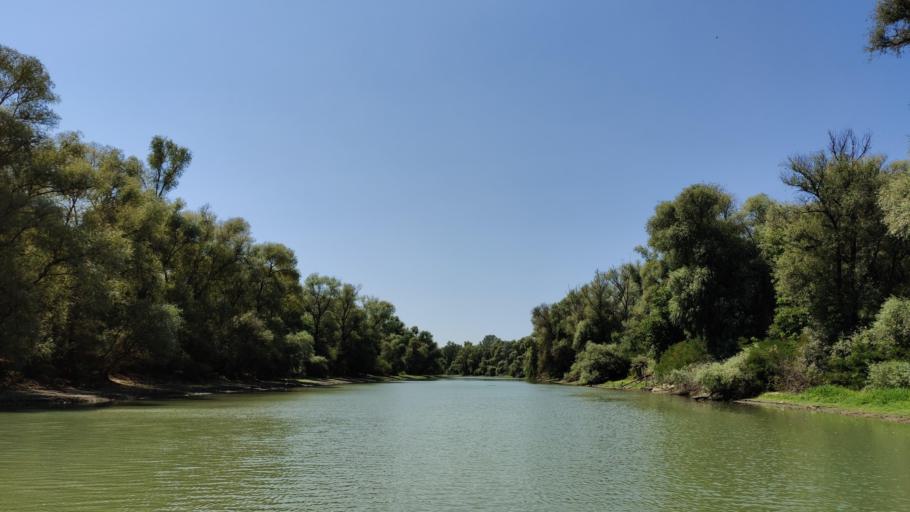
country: RO
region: Tulcea
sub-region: Comuna Nufaru
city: Nufaru
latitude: 45.2284
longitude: 28.8926
